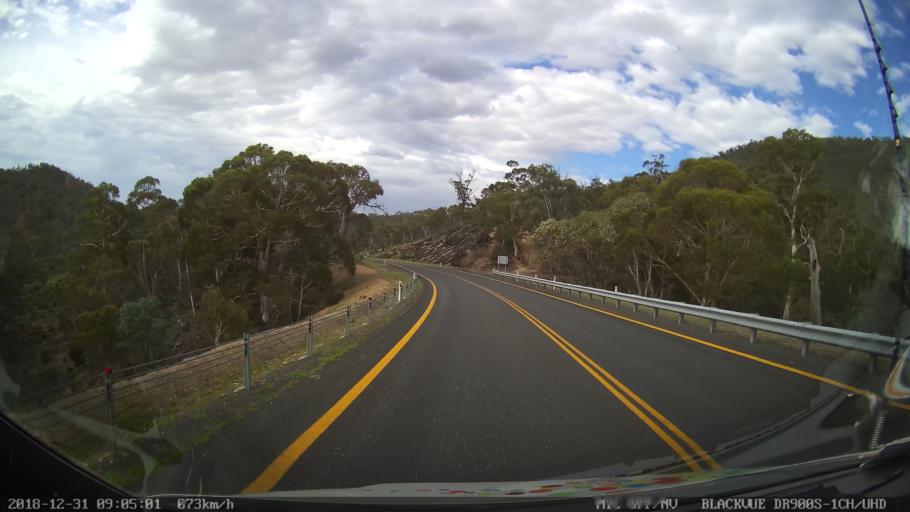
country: AU
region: New South Wales
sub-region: Snowy River
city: Jindabyne
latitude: -36.3591
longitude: 148.5887
